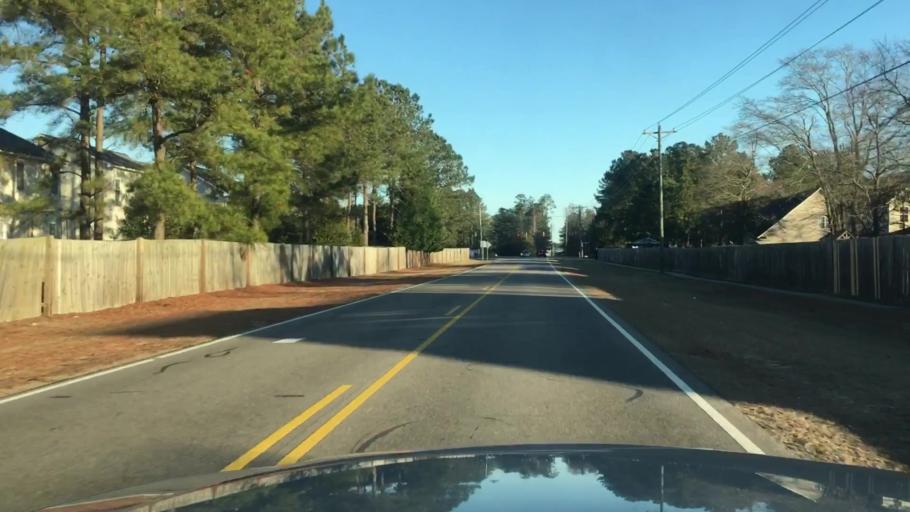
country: US
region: North Carolina
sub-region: Hoke County
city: Rockfish
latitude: 34.9713
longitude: -79.0079
